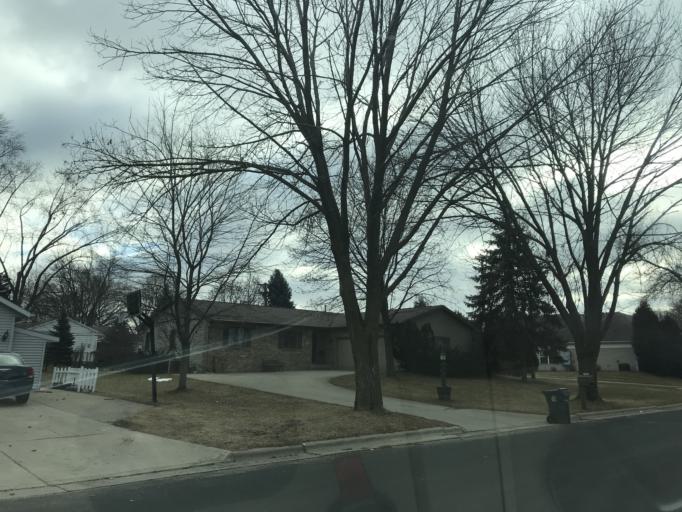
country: US
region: Wisconsin
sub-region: Dane County
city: Monona
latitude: 43.1078
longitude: -89.3061
